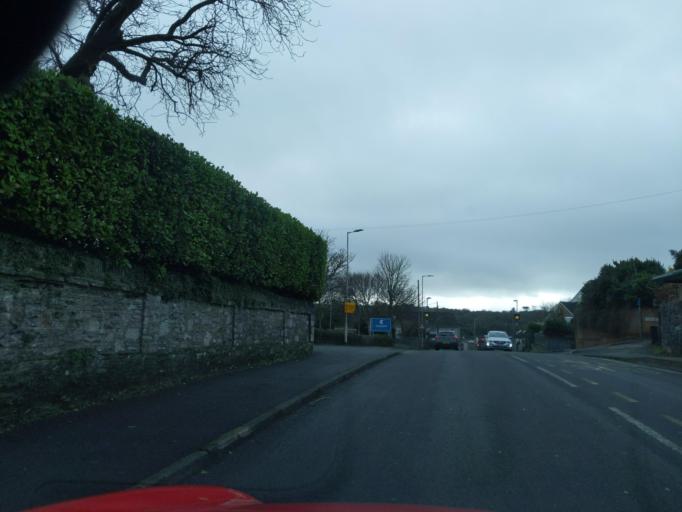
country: GB
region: England
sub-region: Plymouth
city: Plymstock
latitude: 50.3559
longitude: -4.0860
